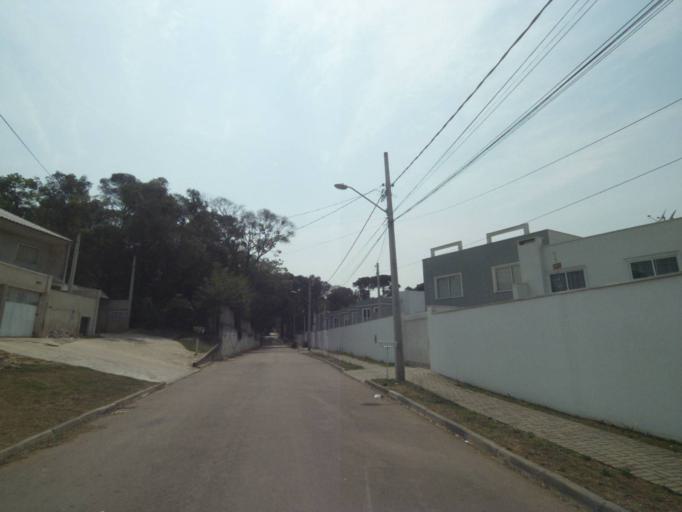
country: BR
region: Parana
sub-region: Pinhais
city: Pinhais
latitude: -25.4845
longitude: -49.2110
